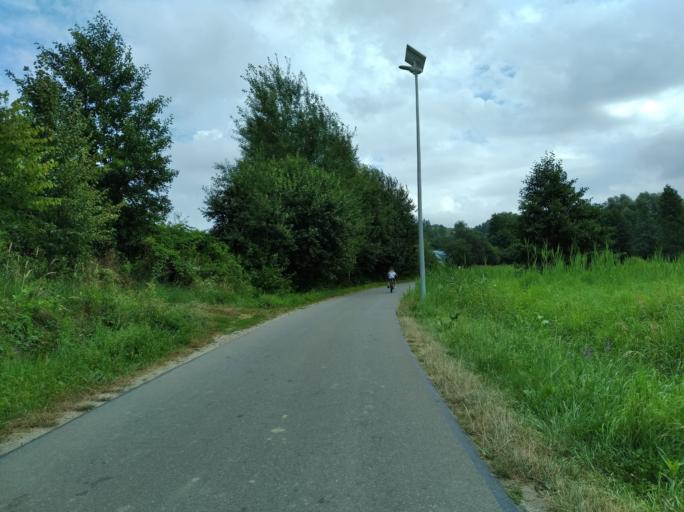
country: PL
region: Subcarpathian Voivodeship
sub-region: Powiat krosnienski
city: Odrzykon
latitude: 49.7400
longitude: 21.7626
